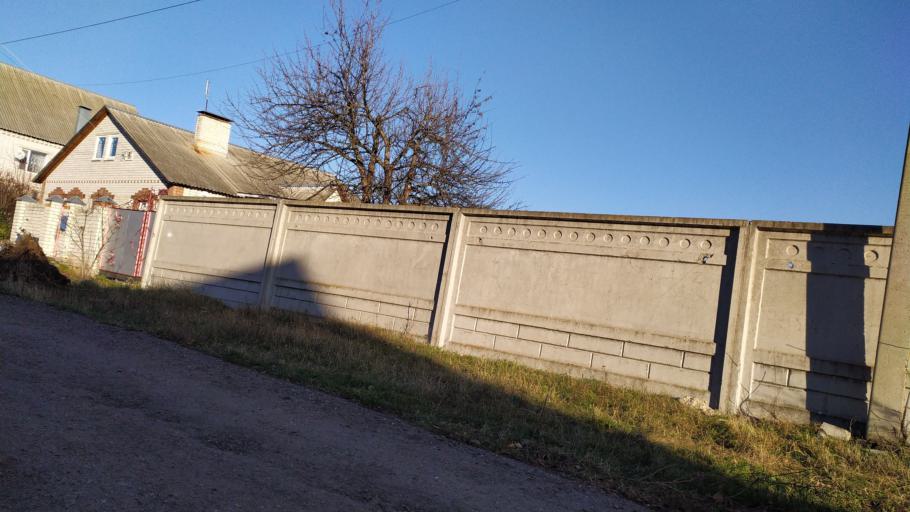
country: RU
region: Kursk
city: Kursk
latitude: 51.6448
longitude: 36.1378
